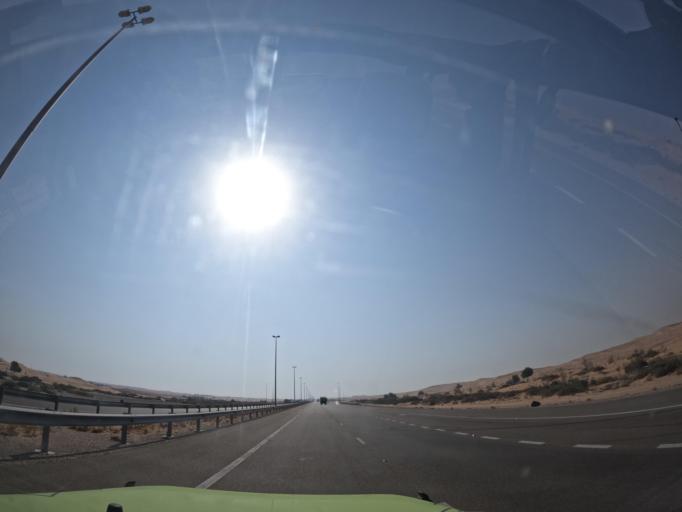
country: OM
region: Al Buraimi
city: Al Buraymi
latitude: 24.5141
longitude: 55.5623
